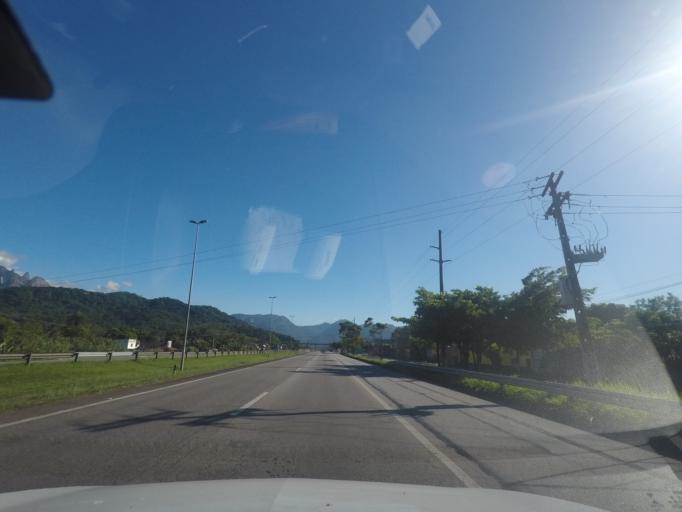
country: BR
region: Rio de Janeiro
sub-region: Guapimirim
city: Guapimirim
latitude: -22.5626
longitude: -42.9980
